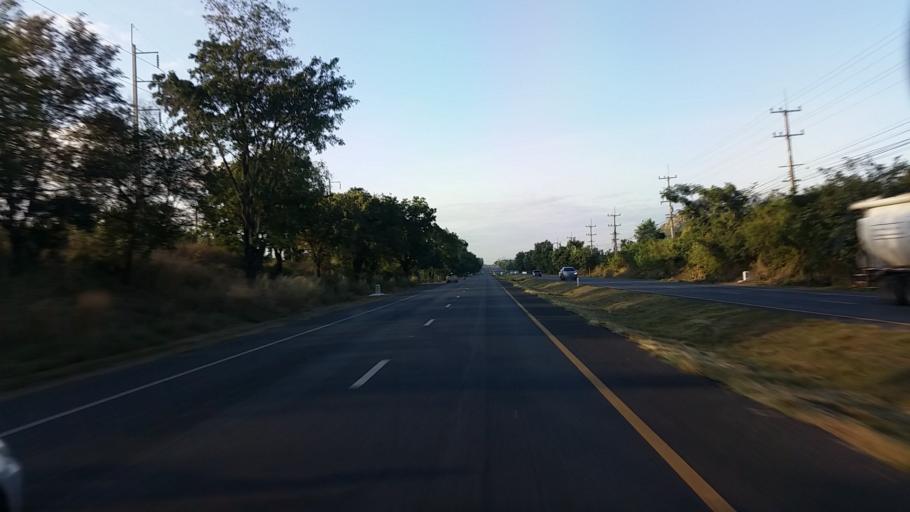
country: TH
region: Lop Buri
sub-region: Amphoe Tha Luang
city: Tha Luang
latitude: 15.1471
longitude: 101.0503
